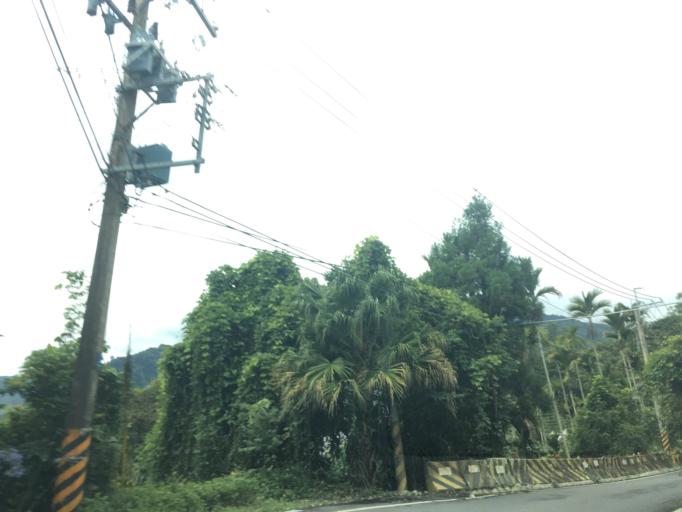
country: TW
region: Taiwan
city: Lugu
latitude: 23.5428
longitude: 120.7156
